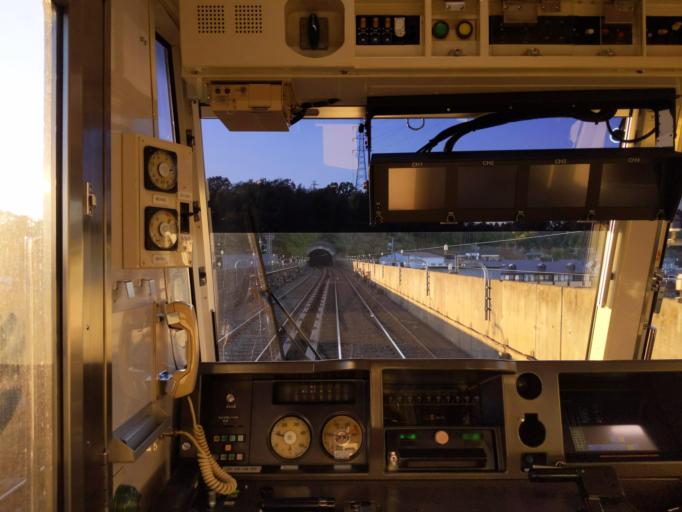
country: JP
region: Kanagawa
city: Yokohama
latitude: 35.5314
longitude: 139.6065
